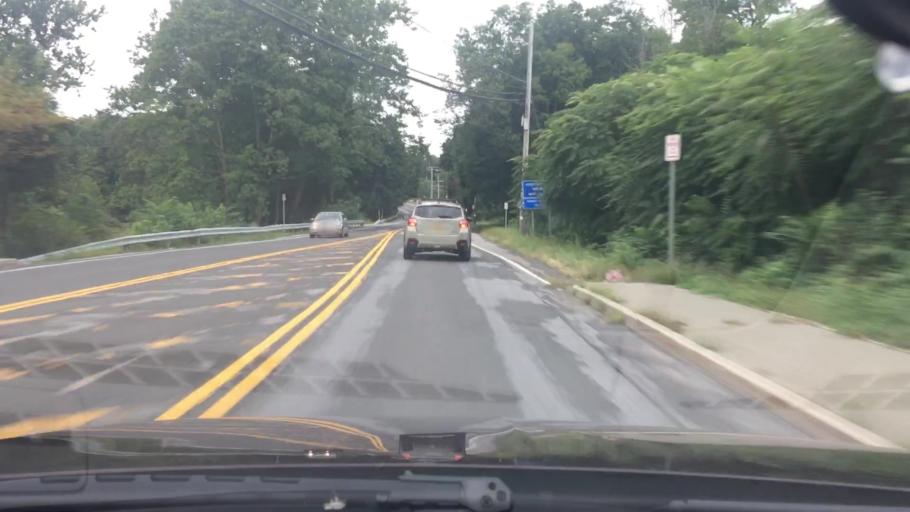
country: US
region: New York
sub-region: Dutchess County
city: Pleasant Valley
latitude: 41.7420
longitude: -73.8302
